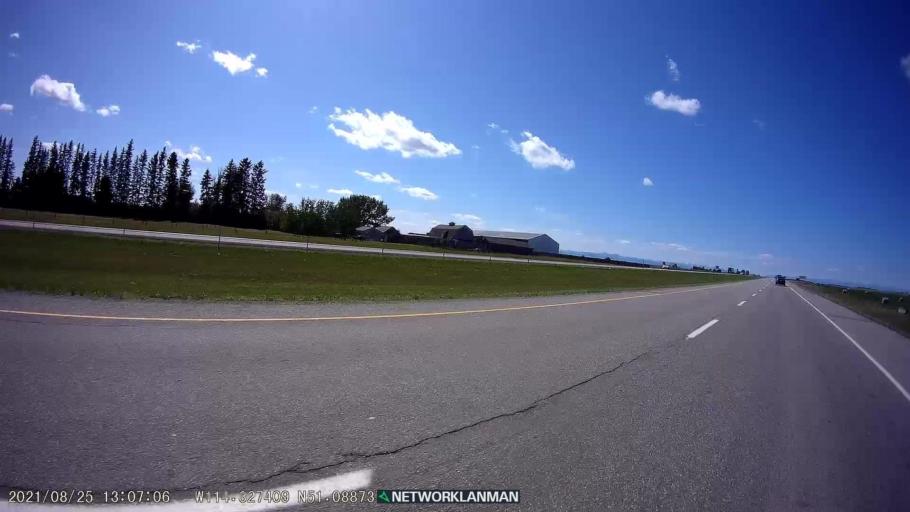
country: CA
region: Alberta
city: Cochrane
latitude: 51.0895
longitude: -114.3284
